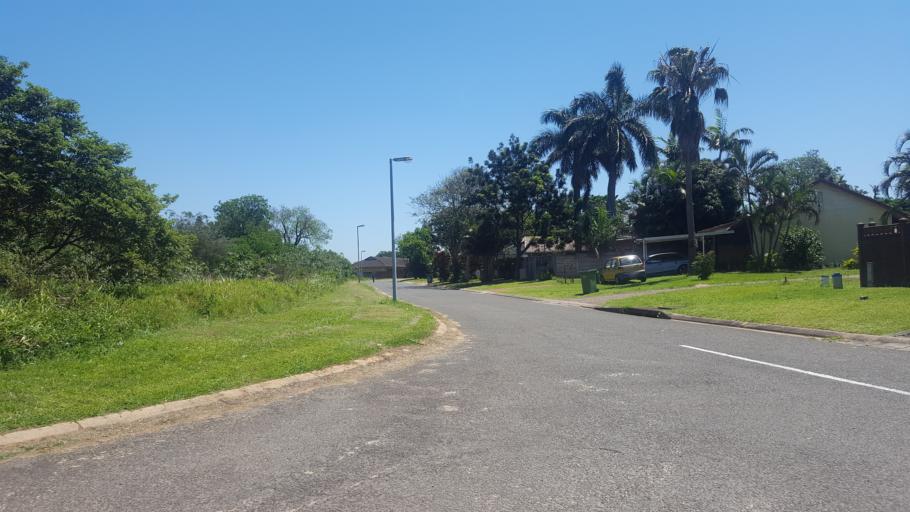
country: ZA
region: KwaZulu-Natal
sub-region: uThungulu District Municipality
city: Richards Bay
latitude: -28.7641
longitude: 32.0700
